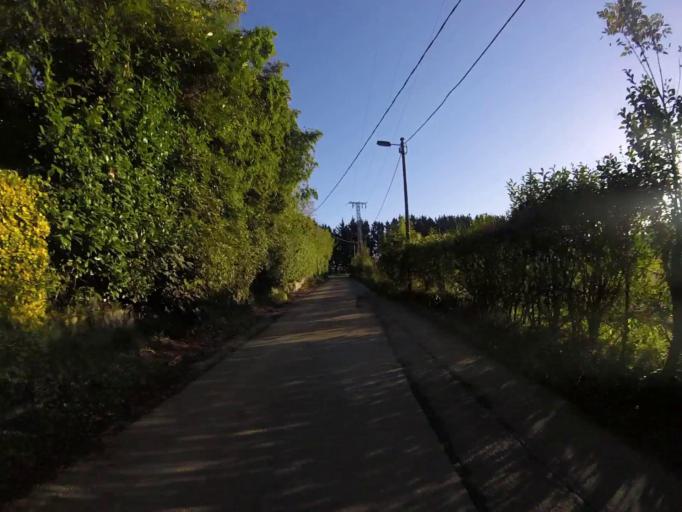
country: ES
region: Basque Country
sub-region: Provincia de Guipuzcoa
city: Lasarte
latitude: 43.2884
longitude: -2.0152
